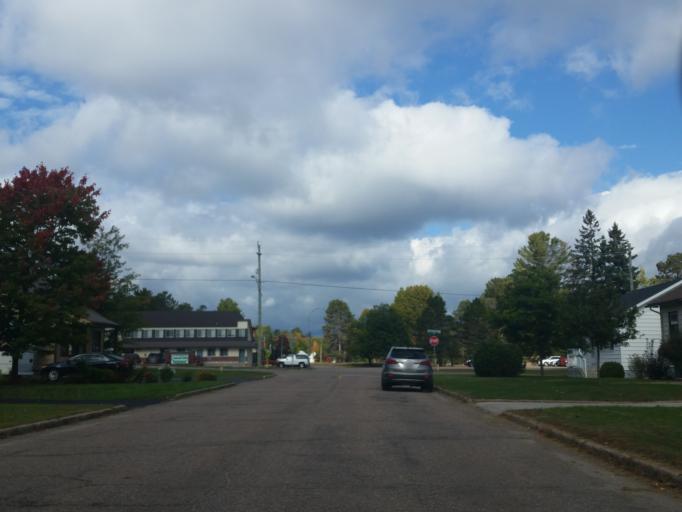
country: CA
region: Ontario
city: Deep River
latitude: 46.0994
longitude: -77.4891
